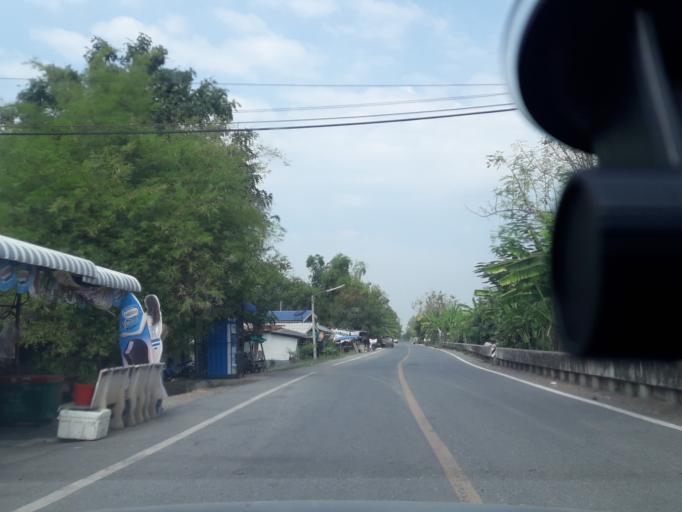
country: TH
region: Pathum Thani
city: Nong Suea
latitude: 14.2241
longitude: 100.8914
